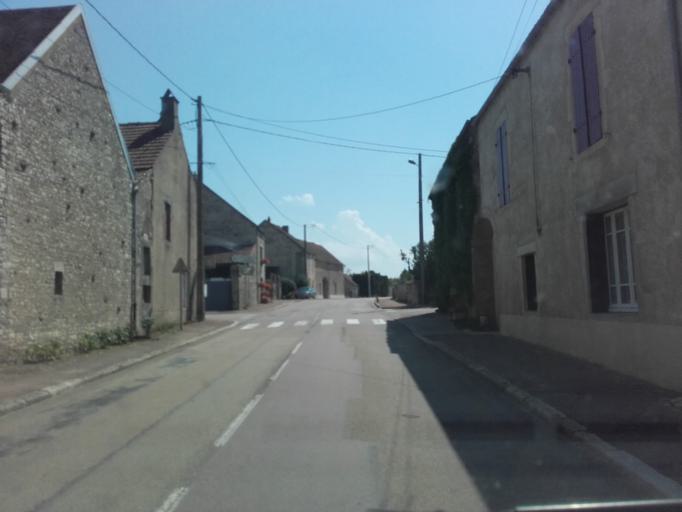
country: FR
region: Bourgogne
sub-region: Departement de l'Yonne
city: Joux-la-Ville
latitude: 47.6706
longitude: 3.8781
